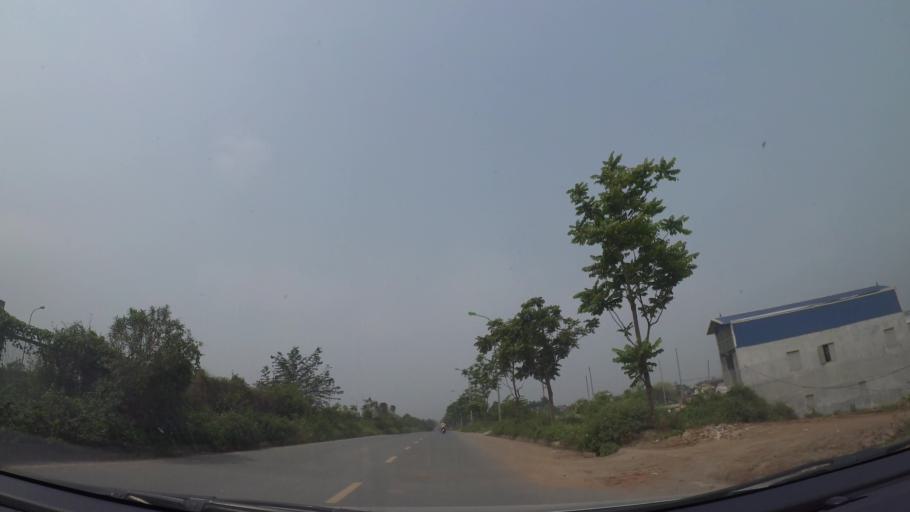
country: VN
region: Ha Noi
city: Quoc Oai
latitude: 20.9959
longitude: 105.5899
